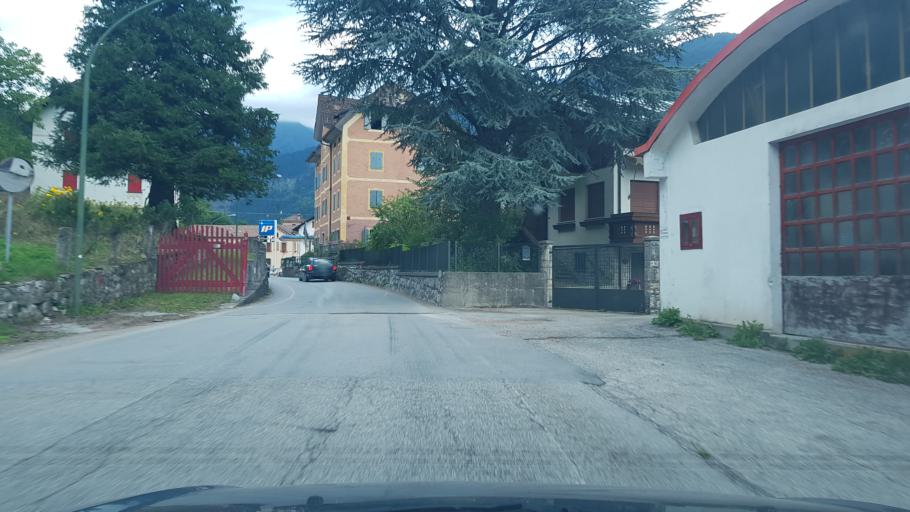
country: IT
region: Friuli Venezia Giulia
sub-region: Provincia di Udine
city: Rigolato
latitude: 46.5482
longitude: 12.8548
